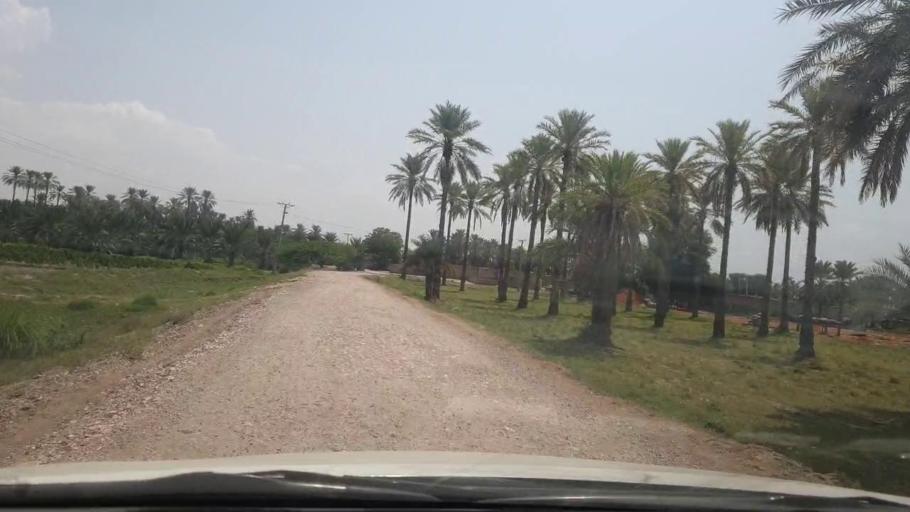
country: PK
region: Sindh
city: Khairpur
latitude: 27.5530
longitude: 68.8277
